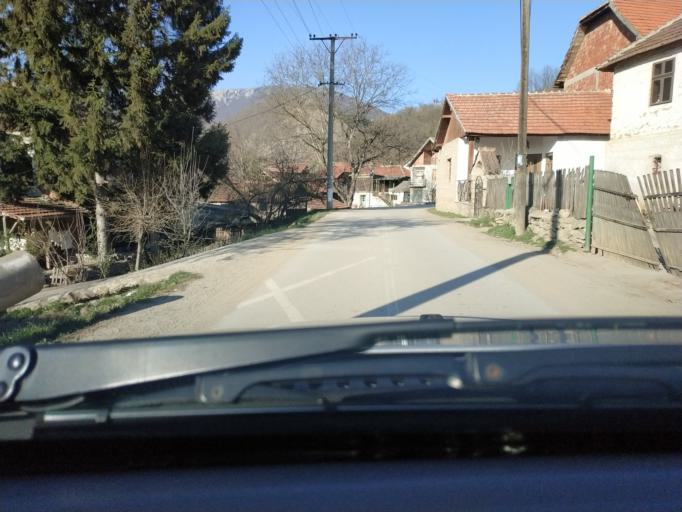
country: RS
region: Central Serbia
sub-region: Nisavski Okrug
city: Aleksinac
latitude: 43.5520
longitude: 21.8141
